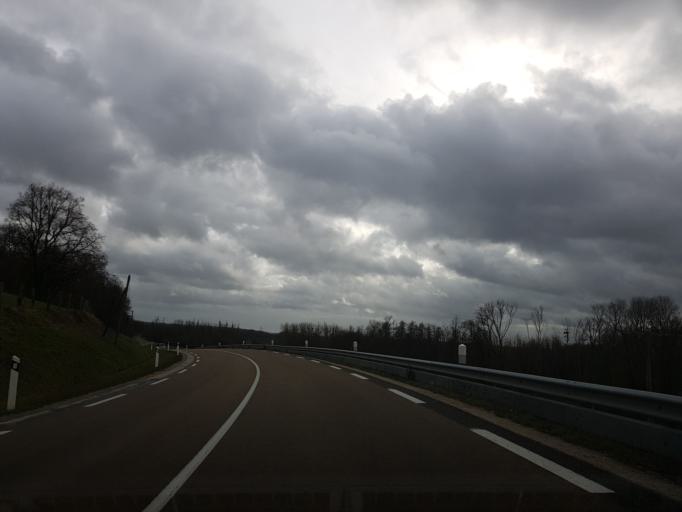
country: FR
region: Champagne-Ardenne
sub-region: Departement de la Haute-Marne
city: Chalindrey
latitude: 47.8250
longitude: 5.4798
